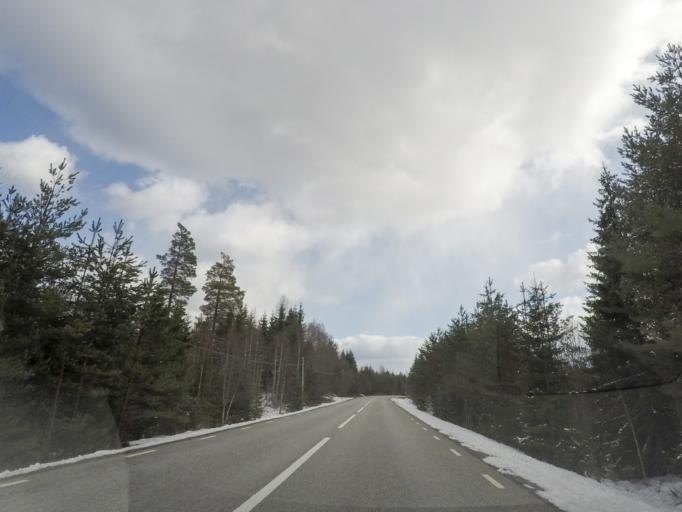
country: SE
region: OErebro
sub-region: Ljusnarsbergs Kommun
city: Kopparberg
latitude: 59.8924
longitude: 15.1093
